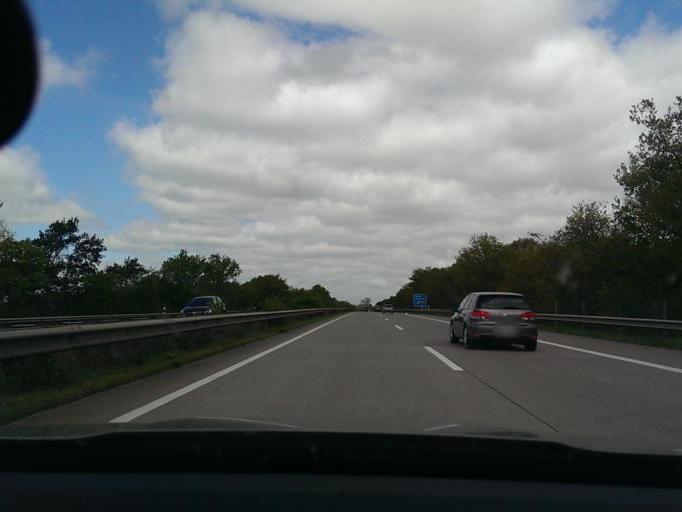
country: DE
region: Lower Saxony
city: Verden
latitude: 52.9552
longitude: 9.2495
